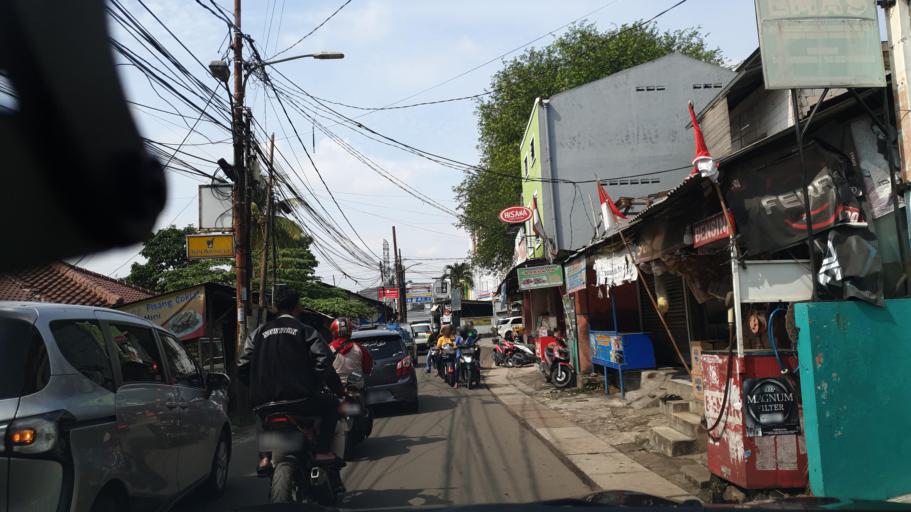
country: ID
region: West Java
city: Pamulang
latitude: -6.3130
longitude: 106.7546
